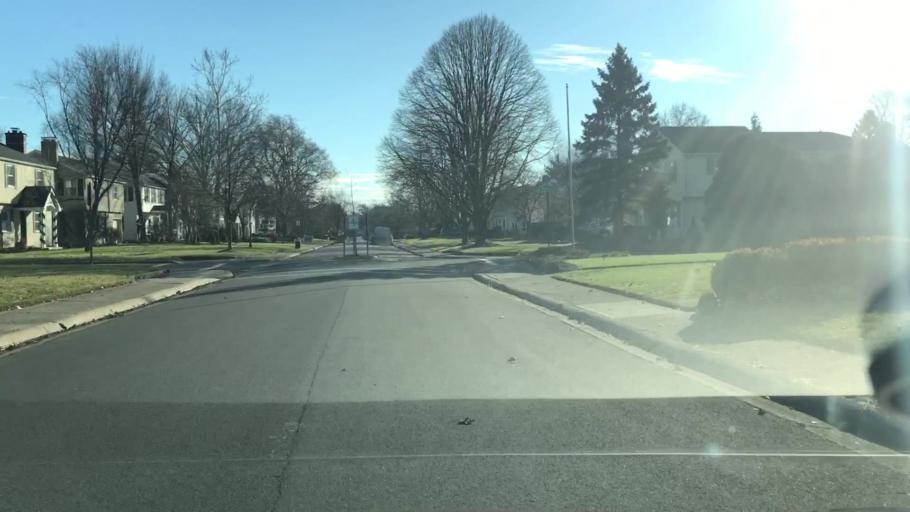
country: US
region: Ohio
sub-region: Franklin County
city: Upper Arlington
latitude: 40.0099
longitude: -83.0569
